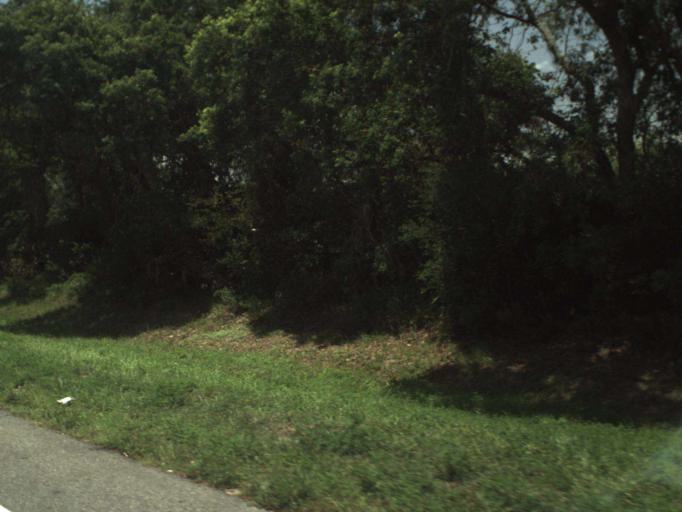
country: US
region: Florida
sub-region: Seminole County
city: Winter Springs
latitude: 28.7049
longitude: -81.2986
